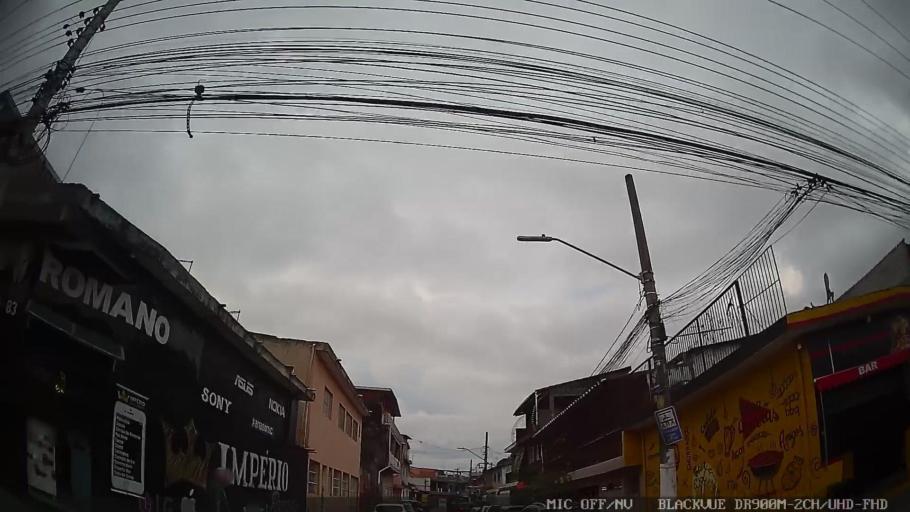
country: BR
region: Sao Paulo
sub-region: Itaquaquecetuba
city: Itaquaquecetuba
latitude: -23.4841
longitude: -46.3844
